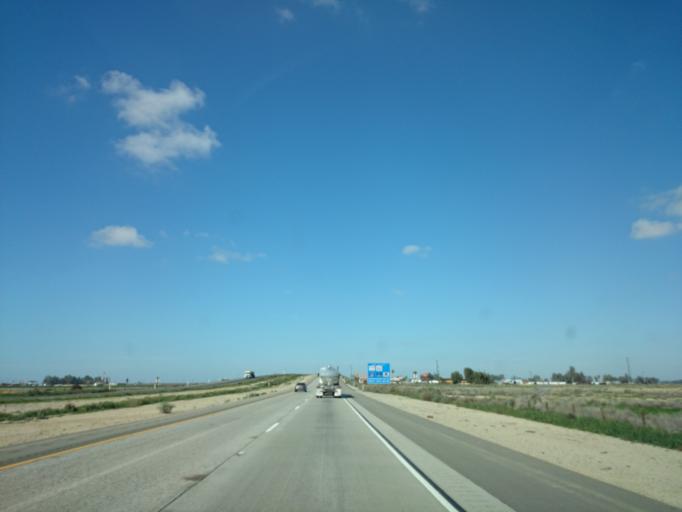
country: US
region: California
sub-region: Kern County
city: Buttonwillow
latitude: 35.3944
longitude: -119.3909
